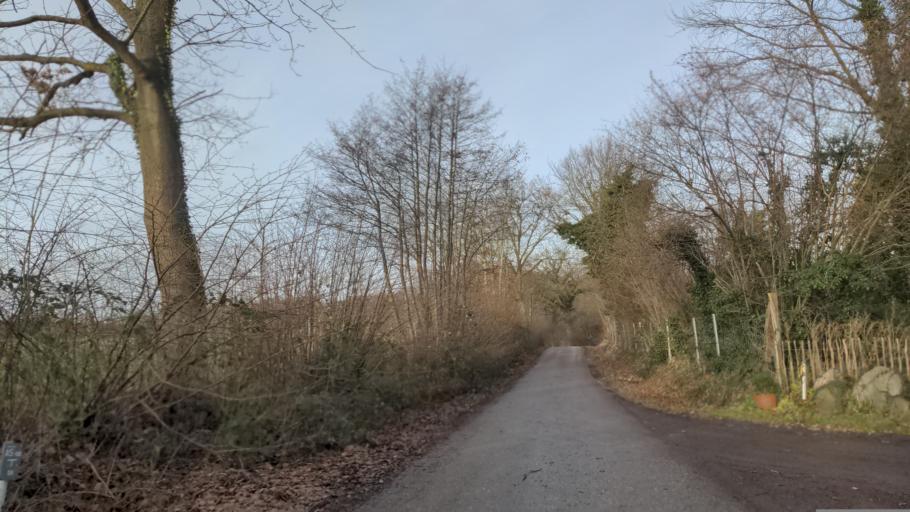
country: DE
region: Schleswig-Holstein
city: Eutin
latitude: 54.1700
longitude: 10.6258
